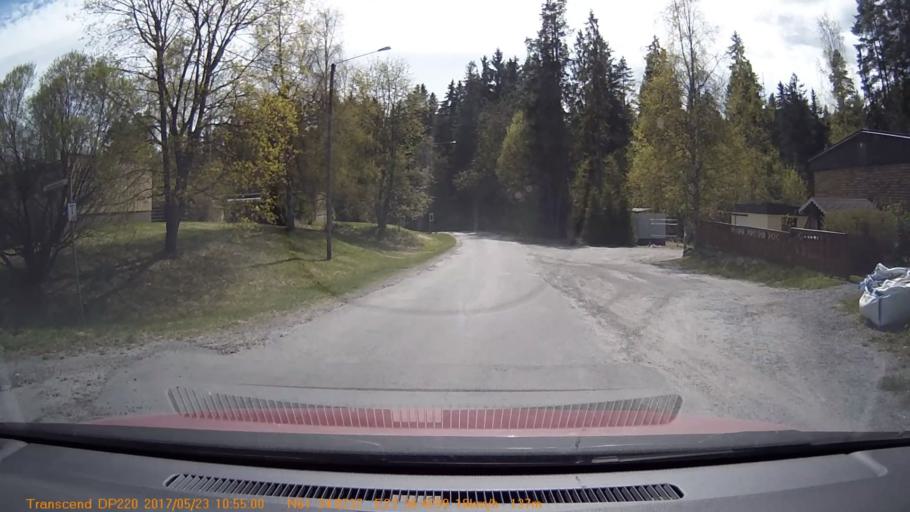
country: FI
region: Pirkanmaa
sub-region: Tampere
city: Yloejaervi
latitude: 61.5681
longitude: 23.6071
